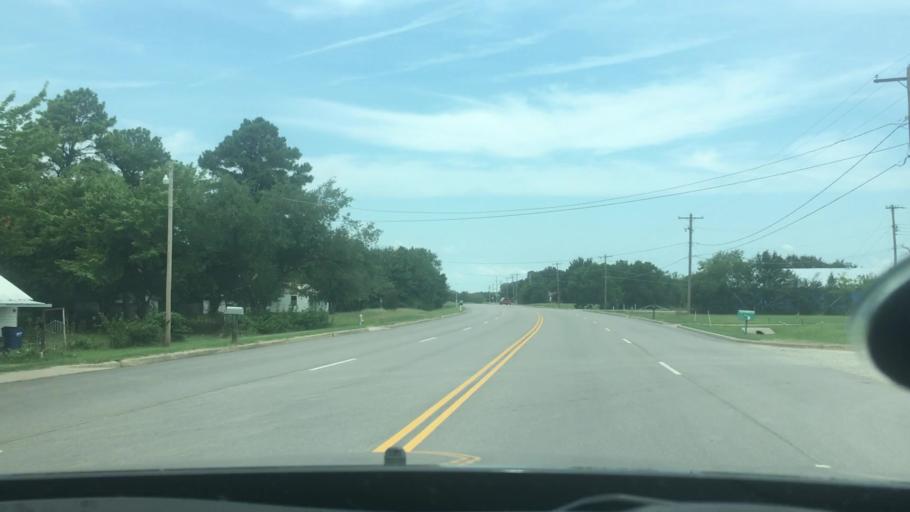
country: US
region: Oklahoma
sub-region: Seminole County
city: Seminole
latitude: 35.2575
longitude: -96.7096
